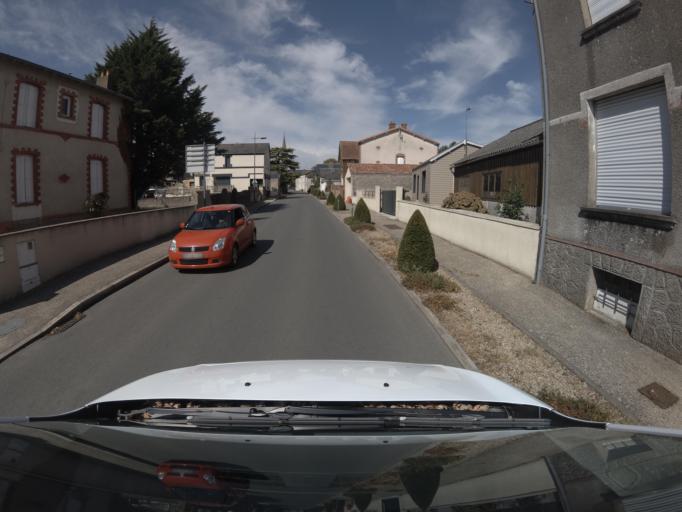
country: FR
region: Poitou-Charentes
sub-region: Departement des Deux-Sevres
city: Nueil-les-Aubiers
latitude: 46.9526
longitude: -0.5907
